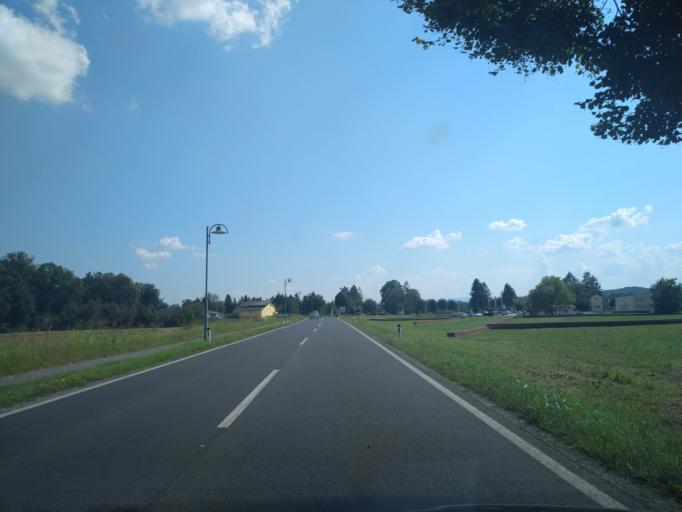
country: AT
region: Styria
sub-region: Politischer Bezirk Leibnitz
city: Gabersdorf
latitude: 46.7711
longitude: 15.5694
